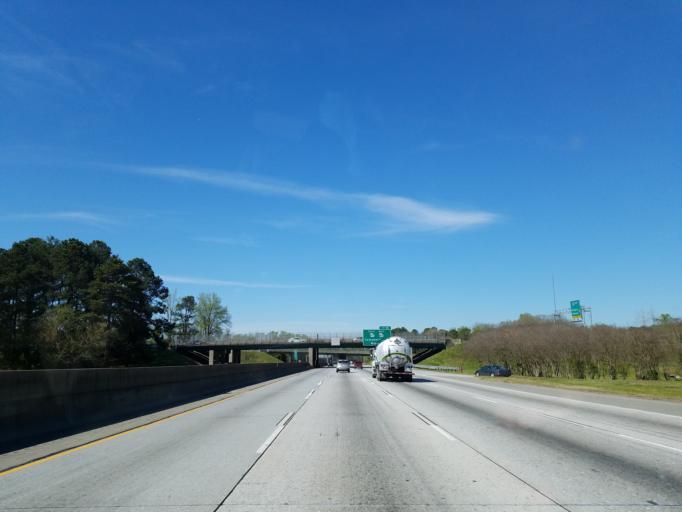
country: US
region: Georgia
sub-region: Fulton County
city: East Point
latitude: 33.6888
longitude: -84.5000
